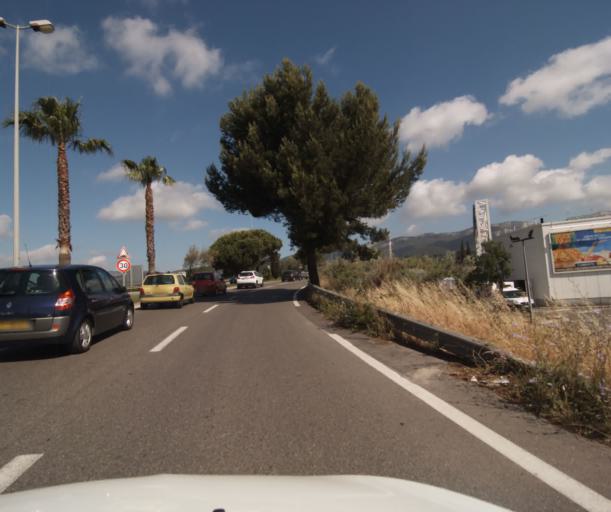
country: FR
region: Provence-Alpes-Cote d'Azur
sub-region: Departement du Var
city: La Seyne-sur-Mer
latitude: 43.1243
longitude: 5.8789
